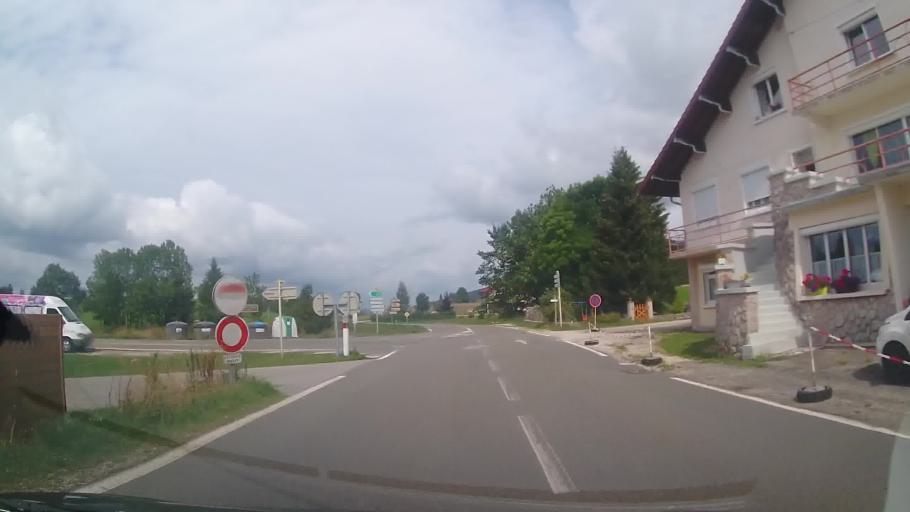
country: FR
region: Franche-Comte
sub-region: Departement du Jura
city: Les Rousses
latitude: 46.4662
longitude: 6.0731
